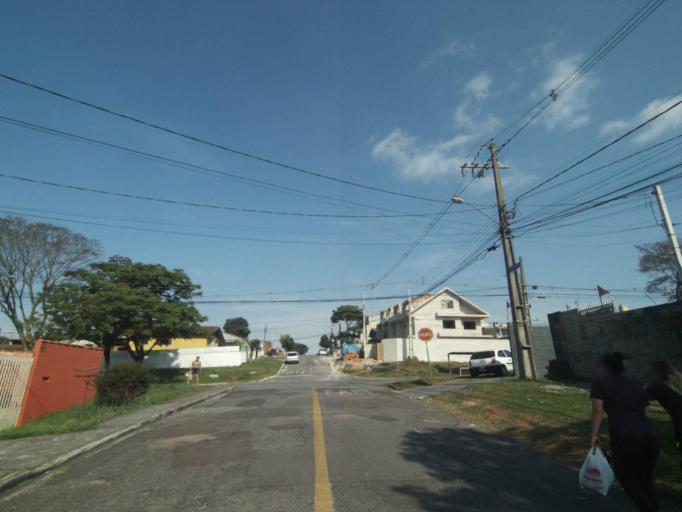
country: BR
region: Parana
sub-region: Curitiba
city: Curitiba
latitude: -25.4808
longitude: -49.3244
